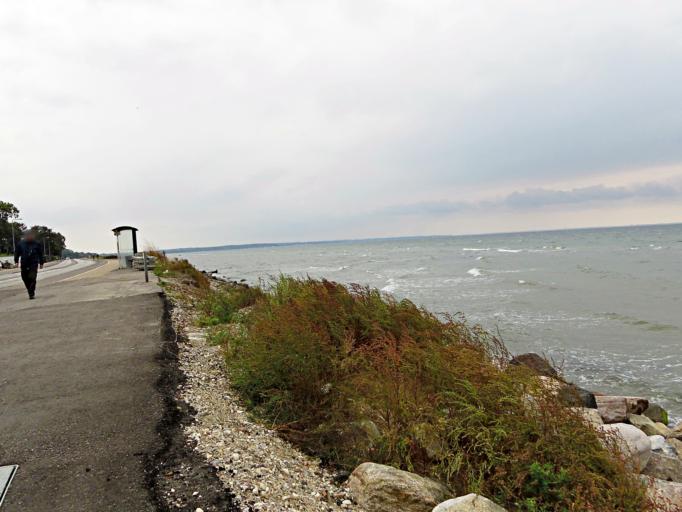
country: DK
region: Capital Region
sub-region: Horsholm Kommune
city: Horsholm
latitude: 55.8964
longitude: 12.5363
